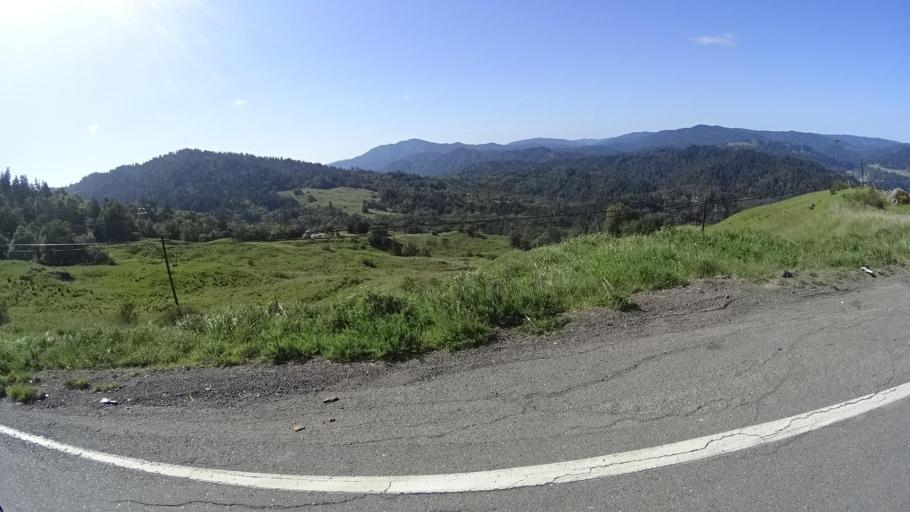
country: US
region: California
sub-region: Humboldt County
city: Redway
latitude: 40.1122
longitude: -123.7735
